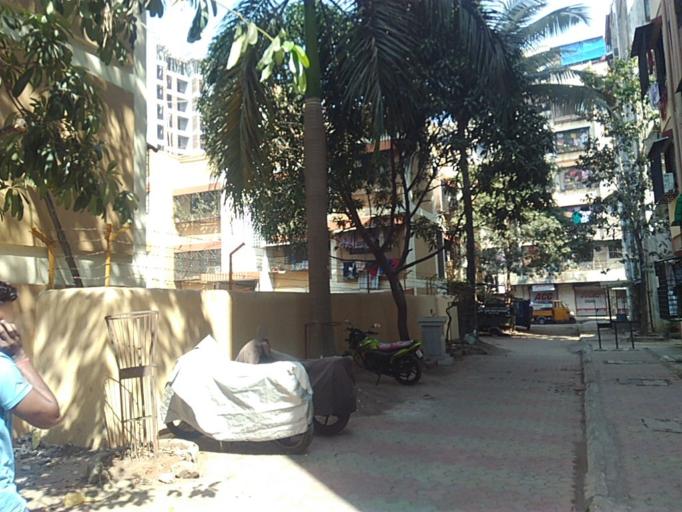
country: IN
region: Maharashtra
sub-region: Thane
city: Bhayandar
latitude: 19.3130
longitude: 72.8557
